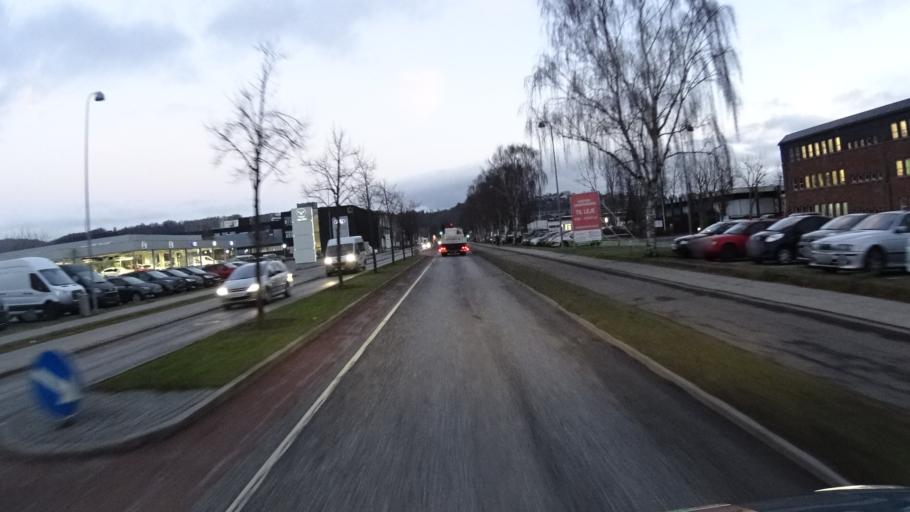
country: DK
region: South Denmark
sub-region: Vejle Kommune
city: Vejle
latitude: 55.7082
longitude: 9.5227
